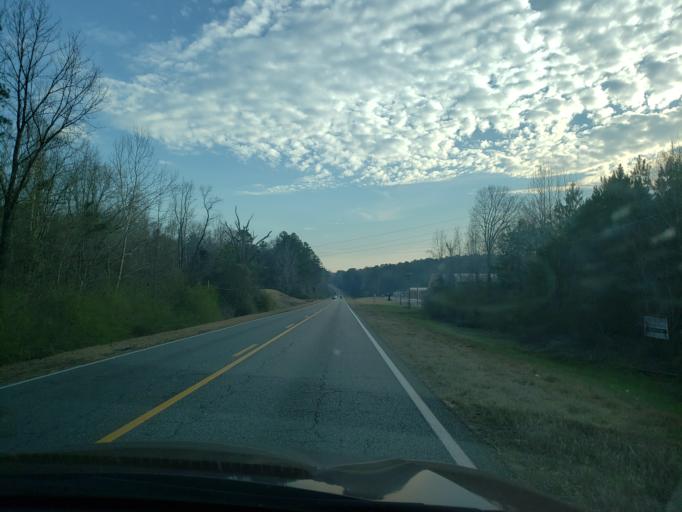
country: US
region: Alabama
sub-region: Hale County
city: Greensboro
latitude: 32.7250
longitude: -87.5905
